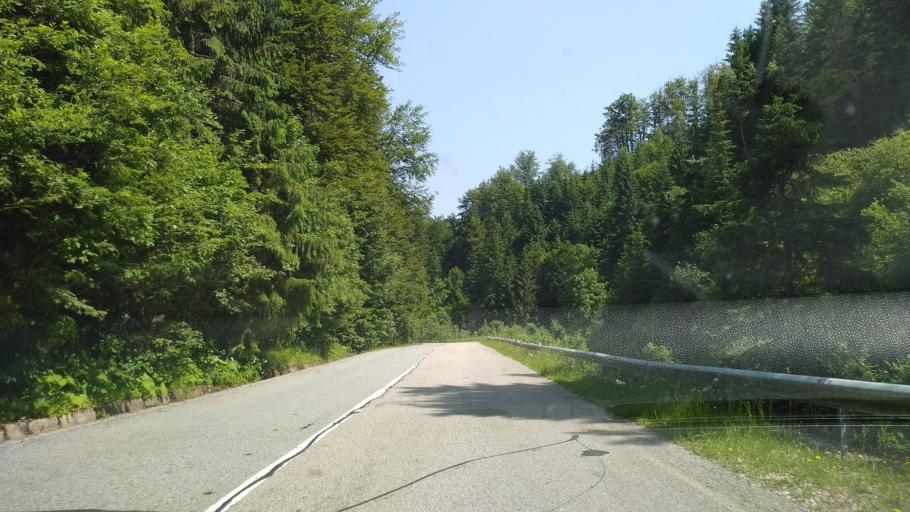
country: RO
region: Gorj
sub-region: Comuna Runcu
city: Valea Mare
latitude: 45.2765
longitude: 22.9376
